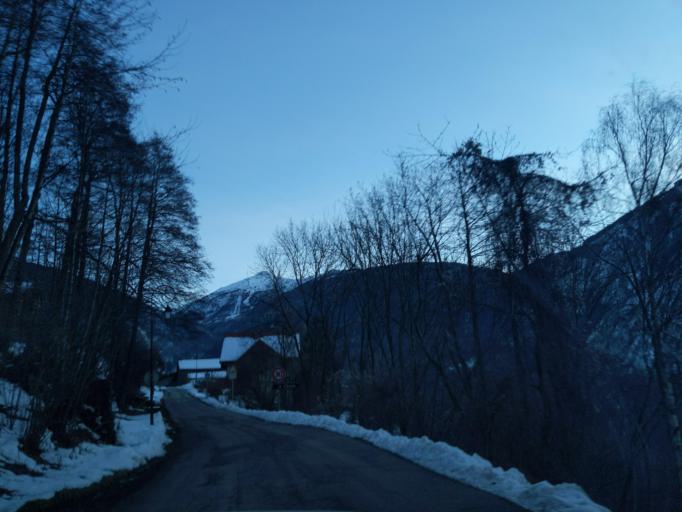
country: FR
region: Rhone-Alpes
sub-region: Departement de la Savoie
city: Saint-Michel-de-Maurienne
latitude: 45.2290
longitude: 6.4675
